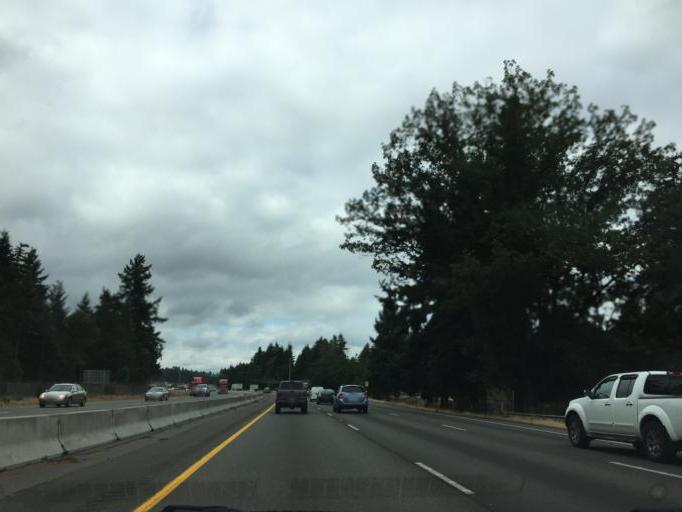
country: US
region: Washington
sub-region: Pierce County
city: Fort Lewis
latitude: 47.1087
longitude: -122.5773
